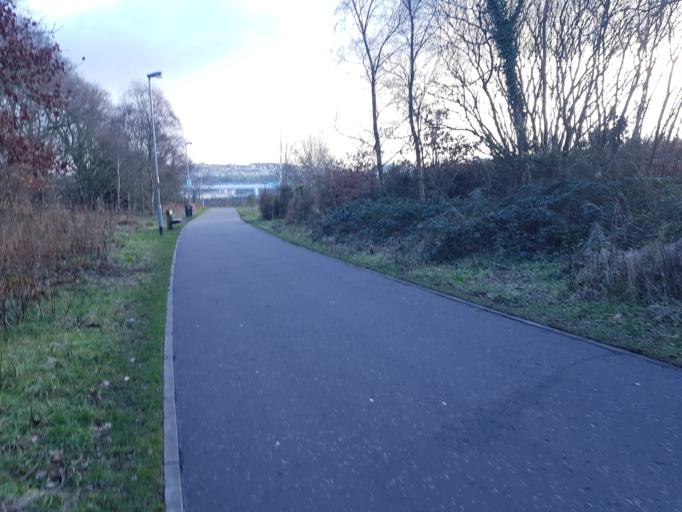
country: GB
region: Northern Ireland
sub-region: City of Derry
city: Derry
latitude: 55.0007
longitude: -7.3148
